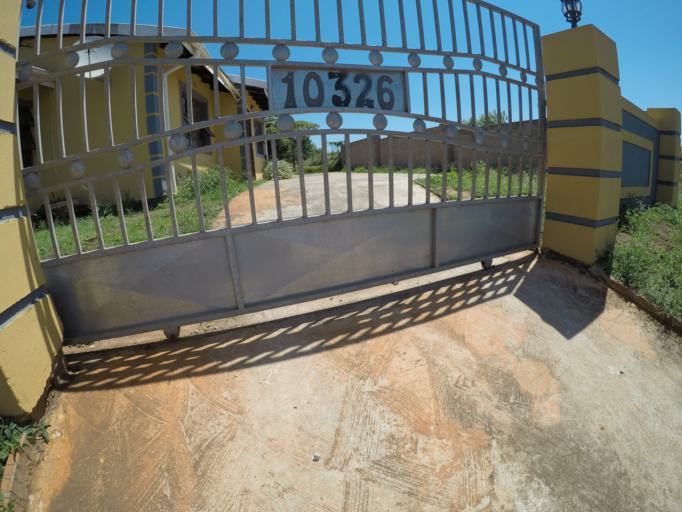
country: ZA
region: KwaZulu-Natal
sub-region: uThungulu District Municipality
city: Empangeni
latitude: -28.7707
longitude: 31.8830
